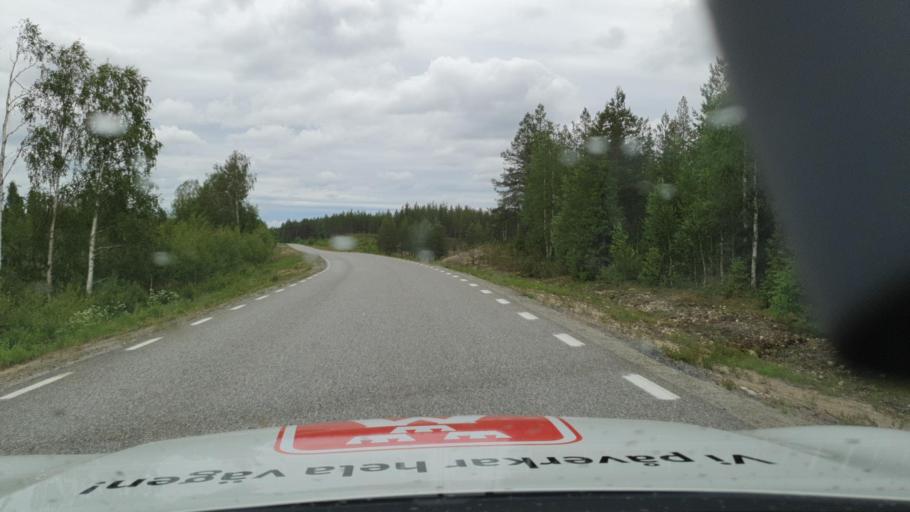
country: SE
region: Vaesterbotten
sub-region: Lycksele Kommun
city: Lycksele
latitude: 64.2206
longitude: 18.2533
